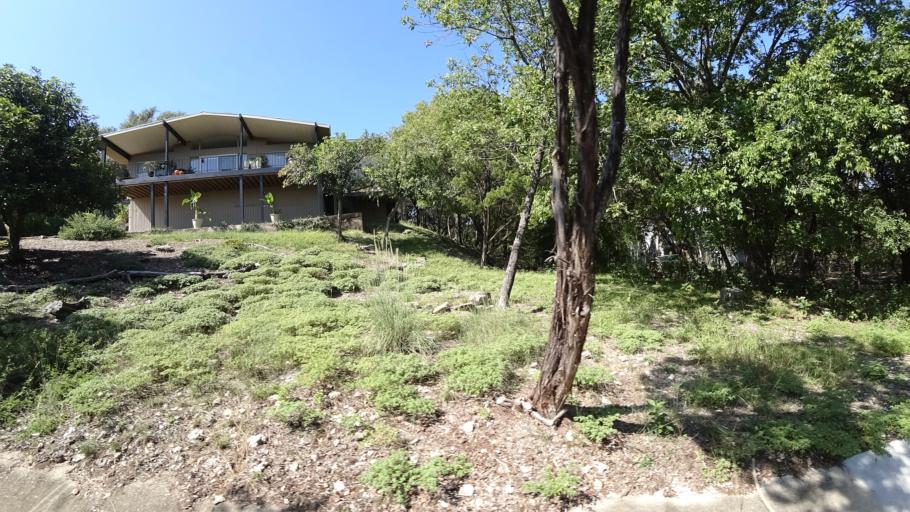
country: US
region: Texas
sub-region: Travis County
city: West Lake Hills
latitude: 30.2983
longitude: -97.7952
